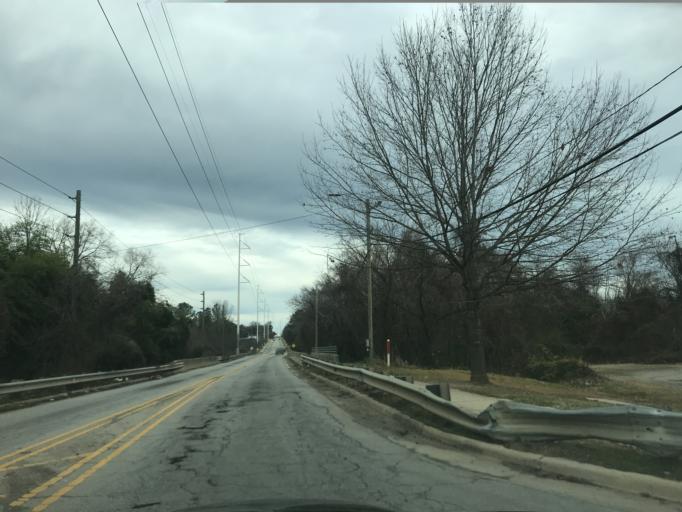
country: US
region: North Carolina
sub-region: Wake County
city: Raleigh
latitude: 35.7570
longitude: -78.6313
